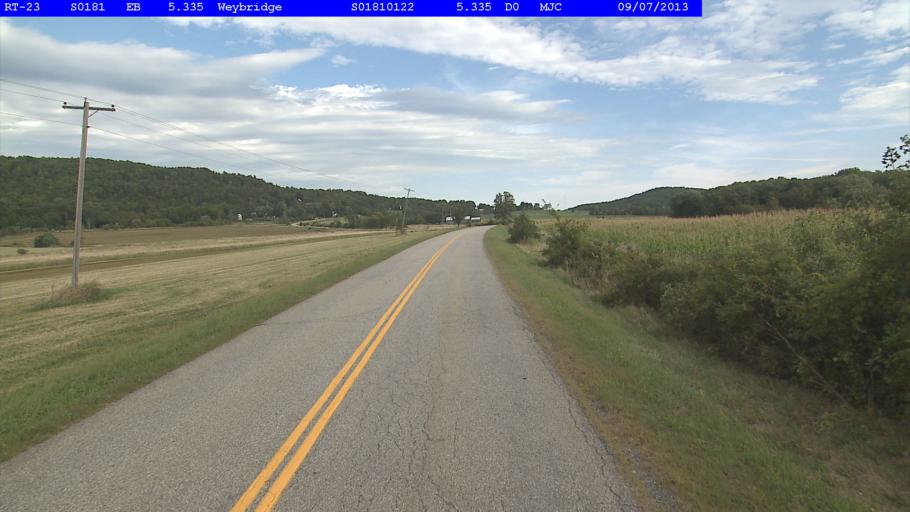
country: US
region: Vermont
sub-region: Addison County
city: Middlebury (village)
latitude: 44.0678
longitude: -73.2502
